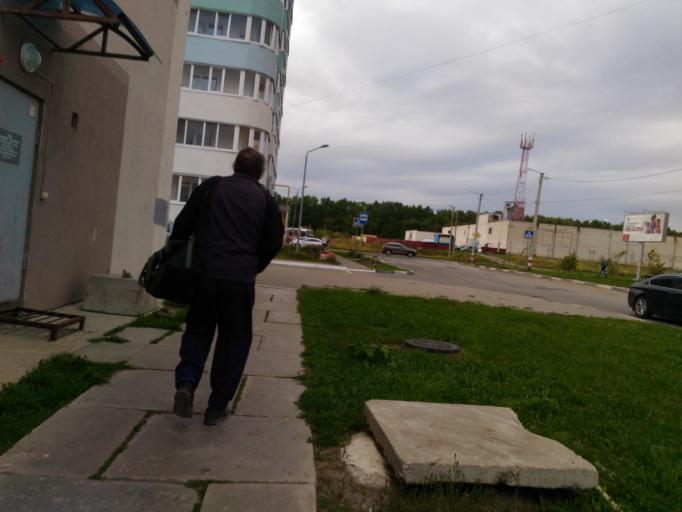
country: RU
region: Ulyanovsk
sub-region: Ulyanovskiy Rayon
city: Ulyanovsk
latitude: 54.3489
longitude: 48.3419
